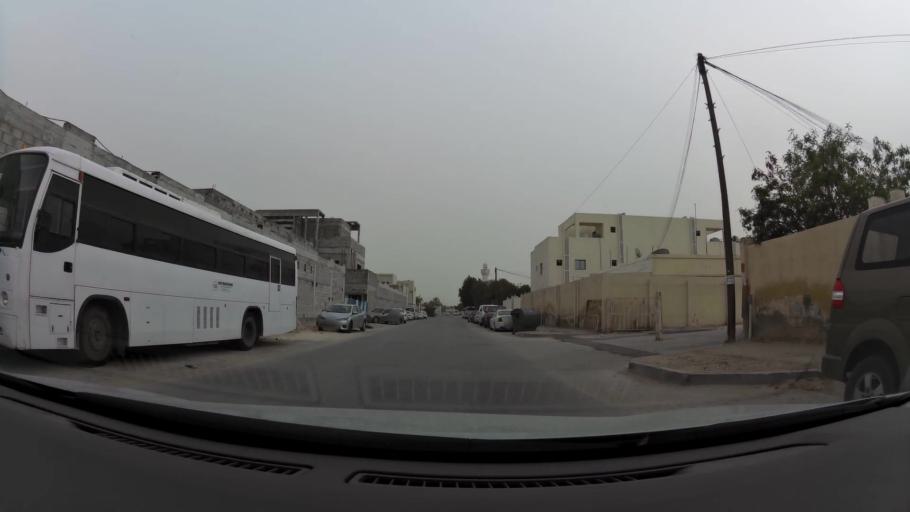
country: QA
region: Baladiyat ad Dawhah
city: Doha
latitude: 25.2596
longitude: 51.4939
